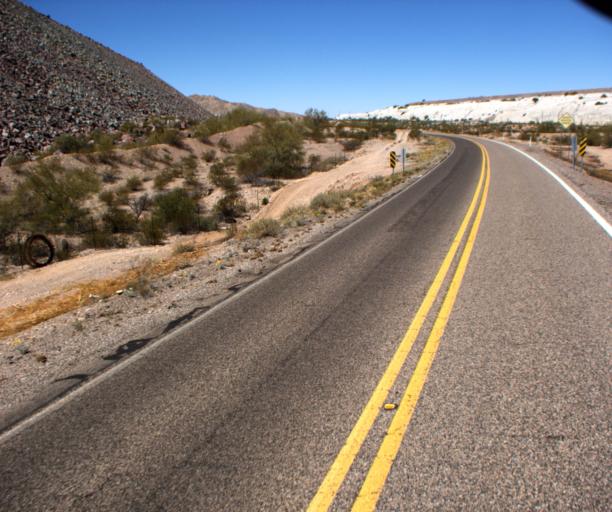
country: US
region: Arizona
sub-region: Pima County
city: Ajo
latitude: 32.3665
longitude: -112.8395
